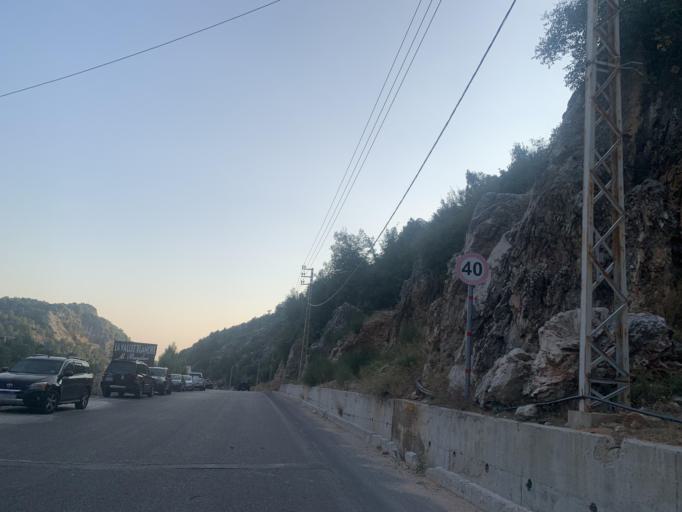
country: LB
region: Mont-Liban
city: Jbail
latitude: 34.1325
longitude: 35.8148
